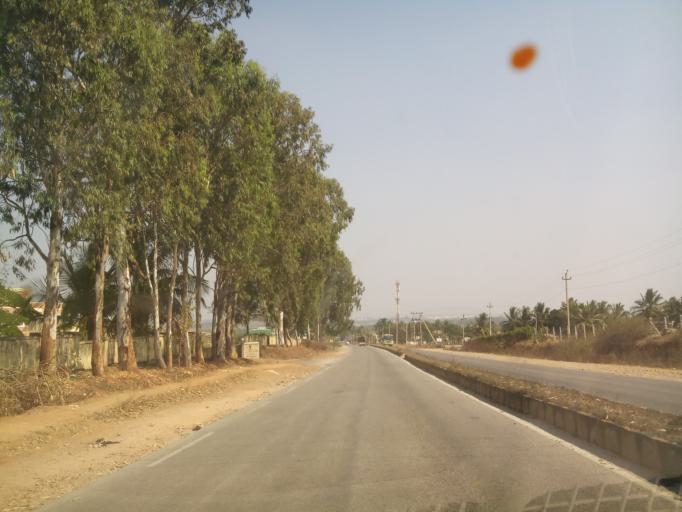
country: IN
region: Karnataka
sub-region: Mandya
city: Shrirangapattana
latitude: 12.4022
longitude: 76.5756
